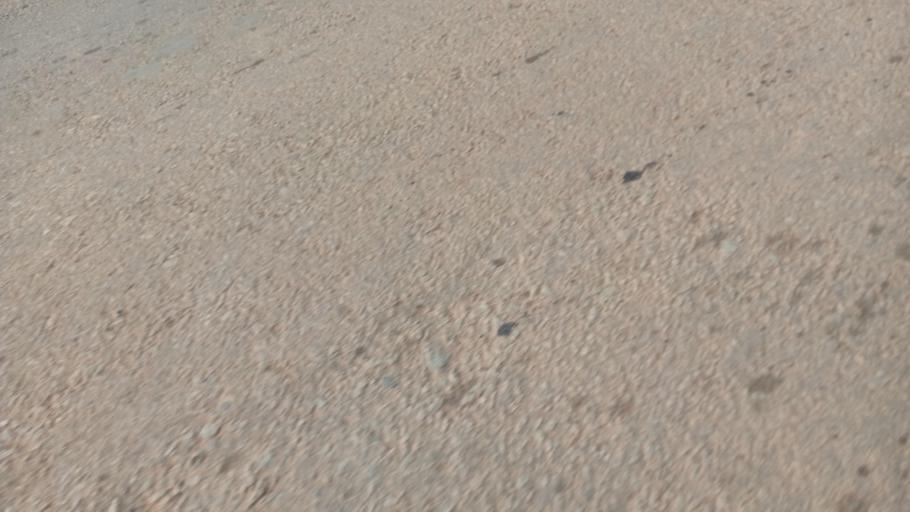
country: SL
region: Southern Province
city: Pujehun
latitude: 7.3582
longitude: -11.7154
